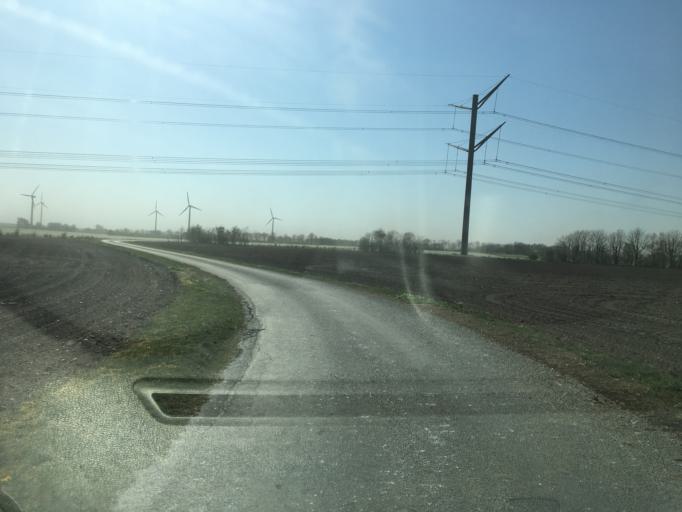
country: DK
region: South Denmark
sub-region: Aabenraa Kommune
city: Rodekro
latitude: 55.1097
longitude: 9.2156
